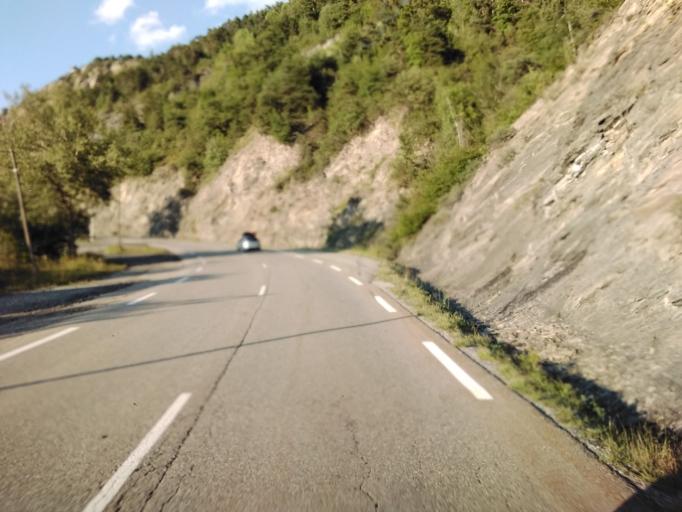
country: FR
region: Provence-Alpes-Cote d'Azur
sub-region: Departement des Alpes-de-Haute-Provence
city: Seyne-les-Alpes
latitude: 44.4454
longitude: 6.3692
